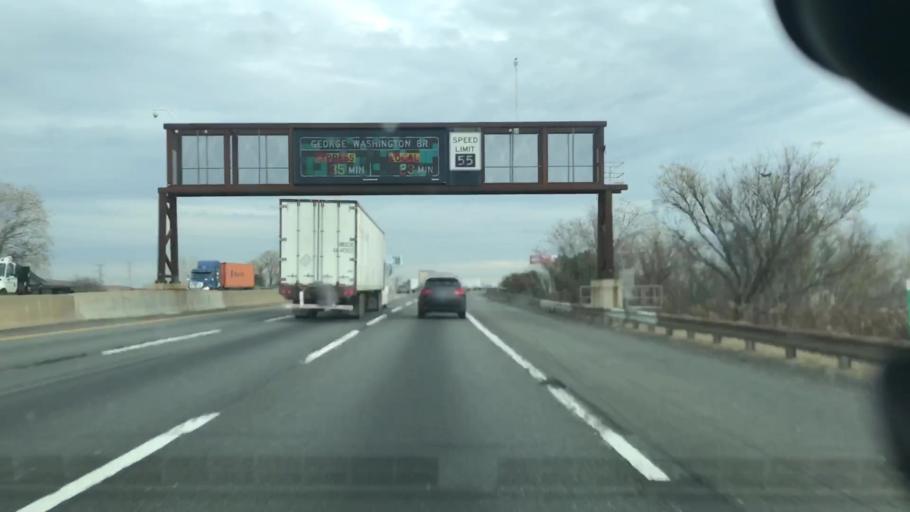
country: US
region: New Jersey
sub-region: Hudson County
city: Kearny
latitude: 40.7591
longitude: -74.1158
